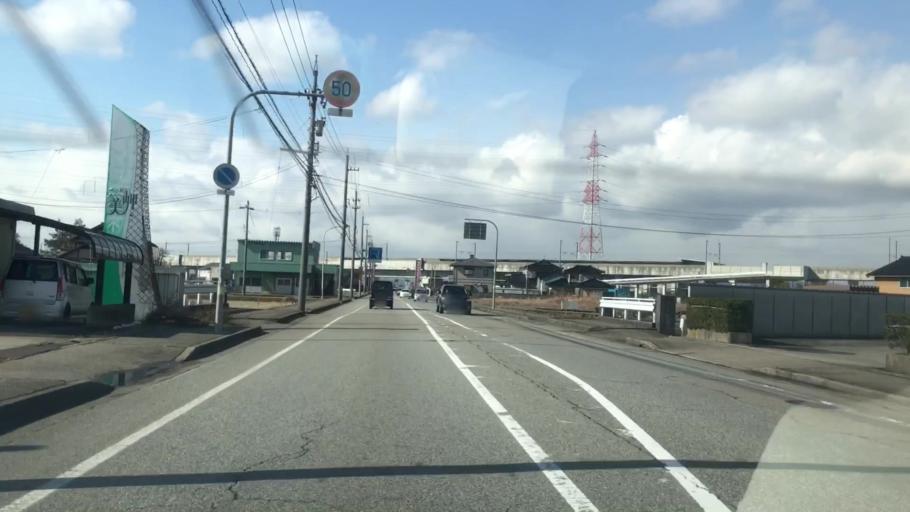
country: JP
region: Toyama
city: Nishishinminato
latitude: 36.7213
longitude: 137.0740
